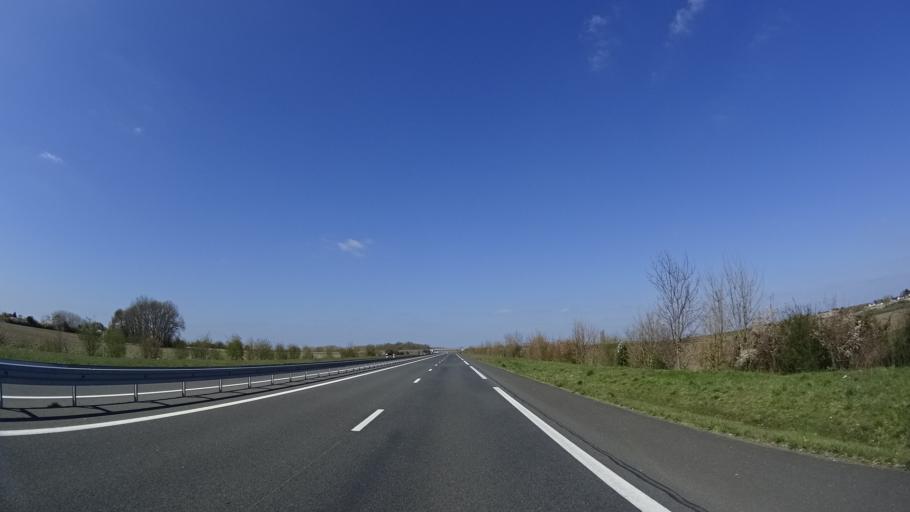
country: FR
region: Pays de la Loire
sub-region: Departement de Maine-et-Loire
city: Saint-Jean
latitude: 47.2789
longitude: -0.3452
